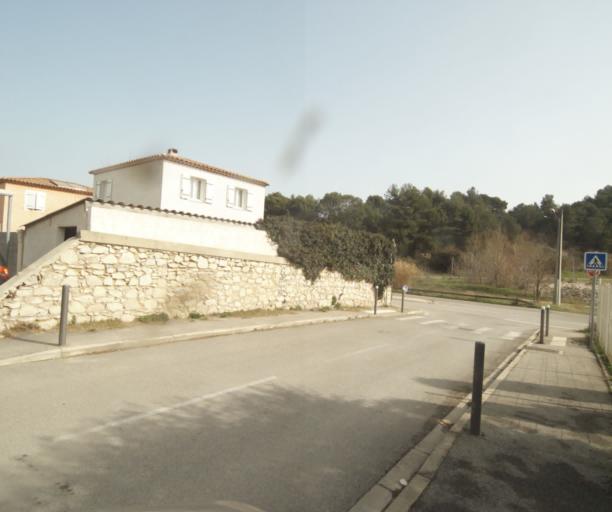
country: FR
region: Provence-Alpes-Cote d'Azur
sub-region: Departement des Bouches-du-Rhone
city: Gardanne
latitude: 43.4475
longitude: 5.4588
